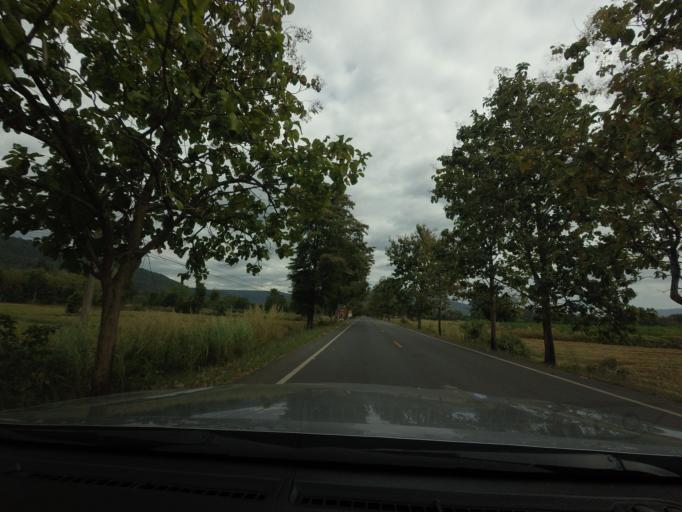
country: TH
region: Phitsanulok
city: Noen Maprang
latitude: 16.7011
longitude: 100.5648
